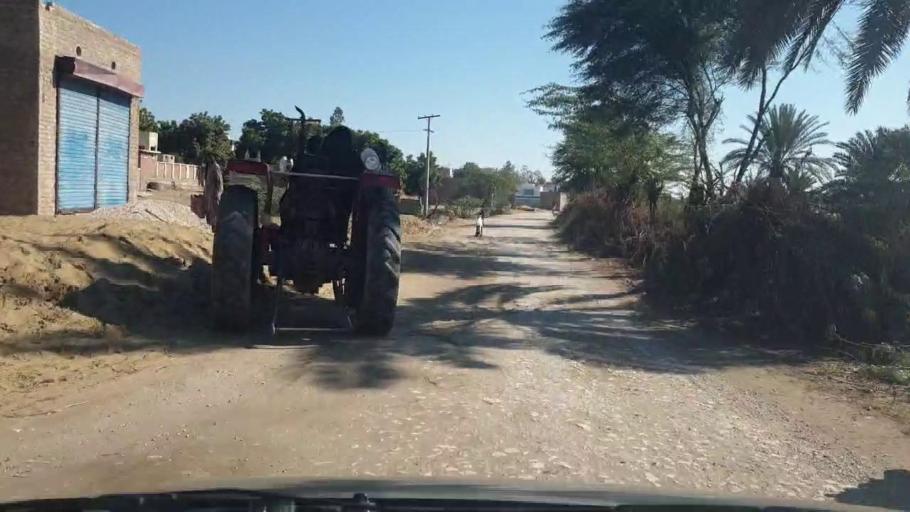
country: PK
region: Sindh
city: Bozdar
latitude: 27.0640
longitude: 68.6227
